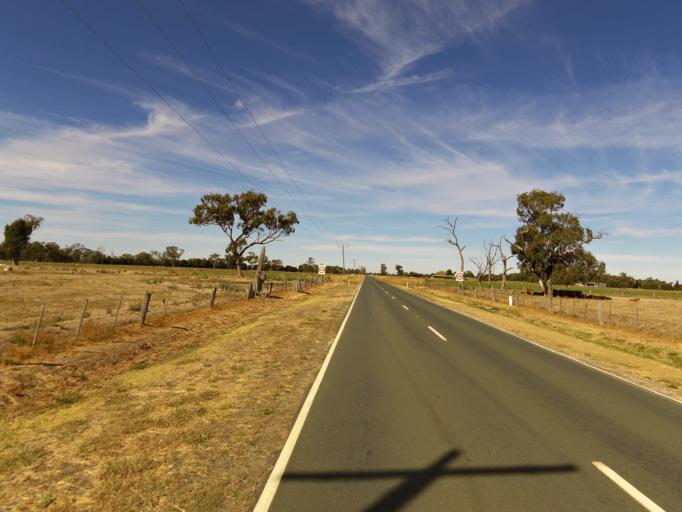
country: AU
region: Victoria
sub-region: Campaspe
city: Echuca
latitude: -36.2775
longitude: 144.5358
